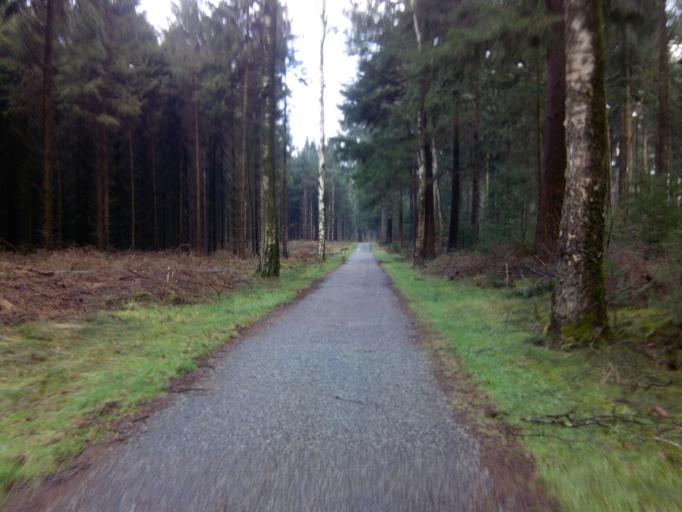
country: NL
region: Utrecht
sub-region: Gemeente Utrechtse Heuvelrug
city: Overberg
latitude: 52.0143
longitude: 5.4969
